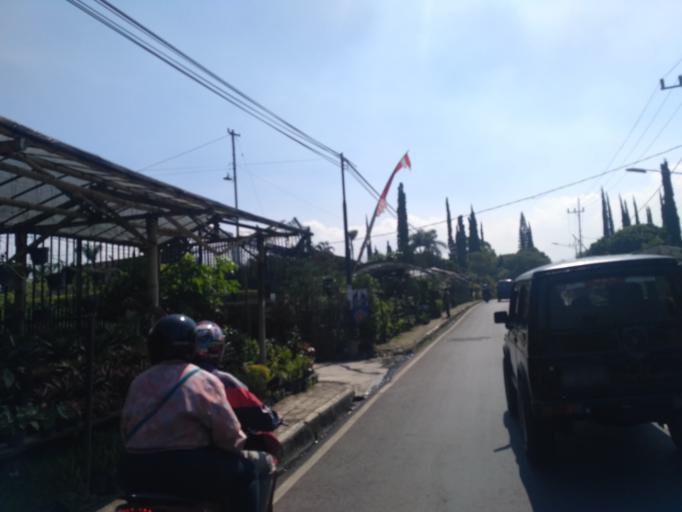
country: ID
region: East Java
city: Batu
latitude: -7.8572
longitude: 112.5268
